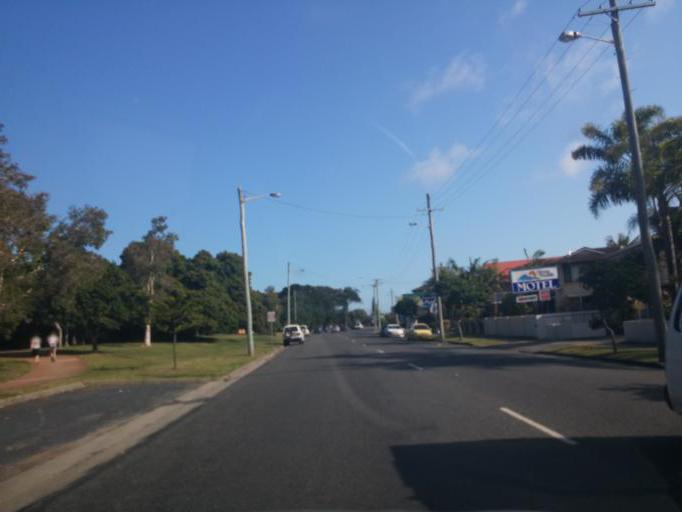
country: AU
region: New South Wales
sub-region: Coffs Harbour
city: Coffs Harbour
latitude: -30.2897
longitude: 153.1381
